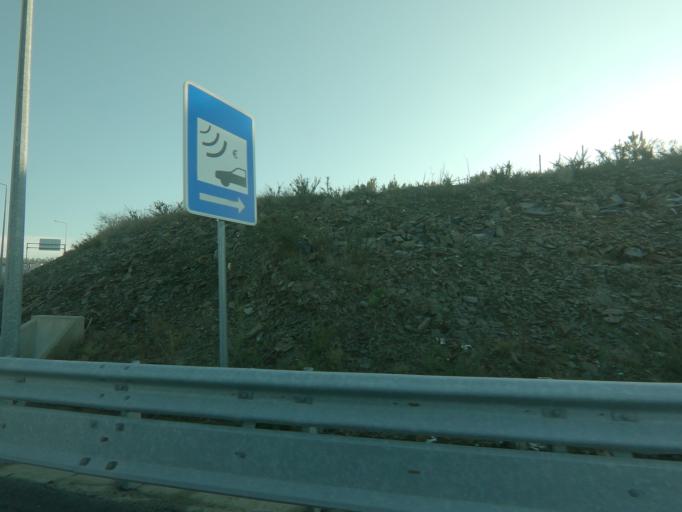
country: PT
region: Vila Real
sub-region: Santa Marta de Penaguiao
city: Santa Marta de Penaguiao
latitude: 41.2824
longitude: -7.8375
